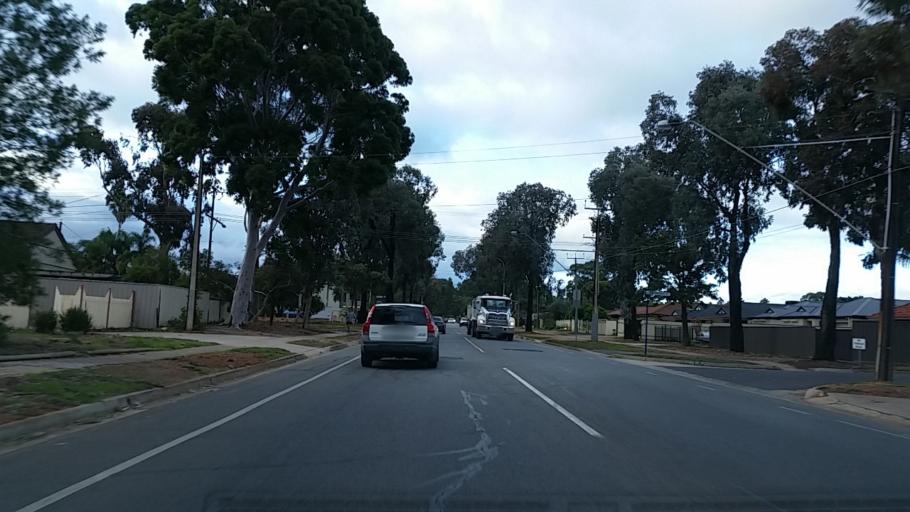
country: AU
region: South Australia
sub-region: Salisbury
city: Salisbury
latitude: -34.7625
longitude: 138.6571
